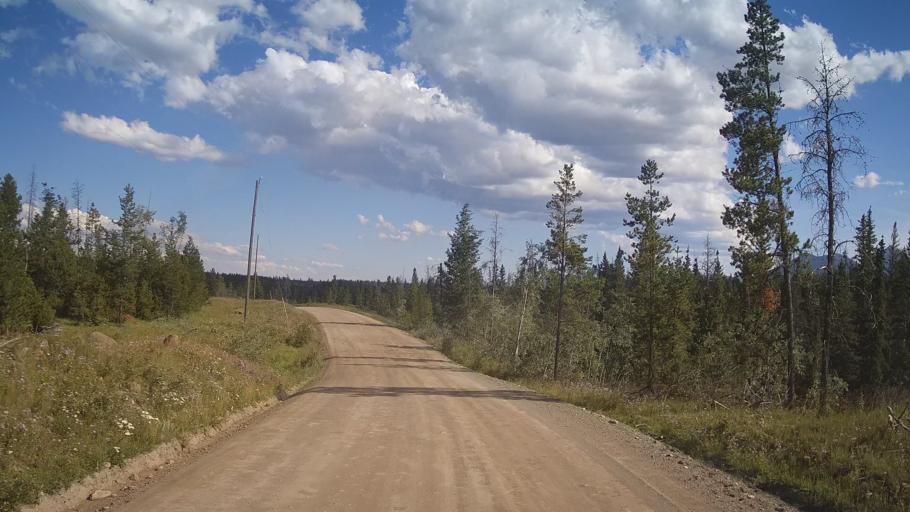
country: CA
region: British Columbia
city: Lillooet
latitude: 51.2886
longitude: -121.7516
